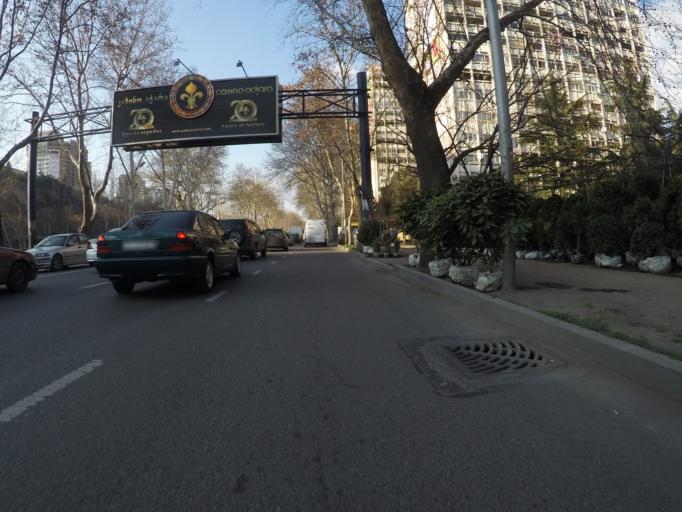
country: GE
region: T'bilisi
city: Tbilisi
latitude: 41.7180
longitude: 44.7875
